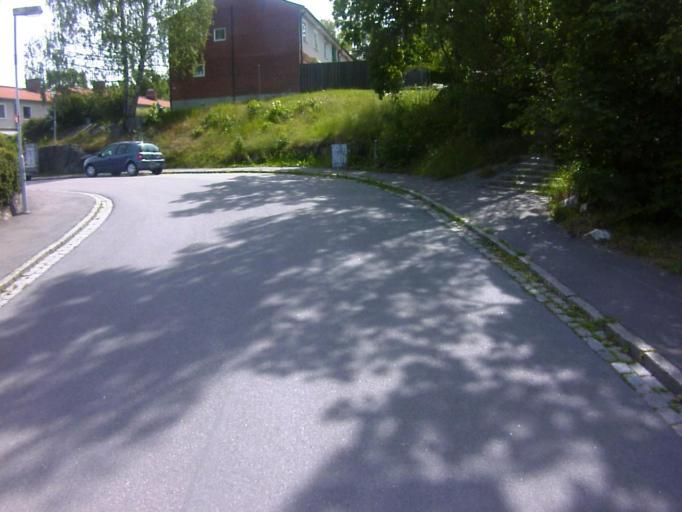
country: SE
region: Soedermanland
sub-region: Eskilstuna Kommun
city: Eskilstuna
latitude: 59.3615
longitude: 16.5276
